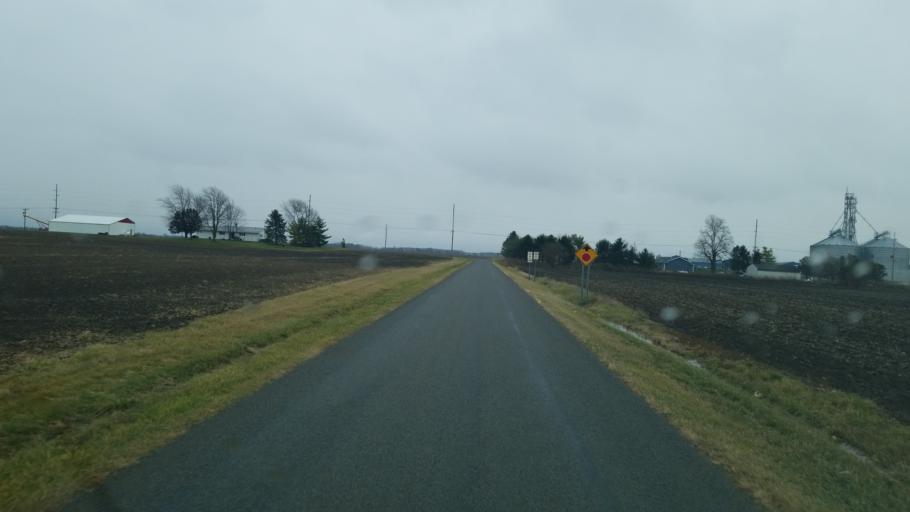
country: US
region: Ohio
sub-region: Logan County
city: Northwood
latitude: 40.4359
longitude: -83.5639
